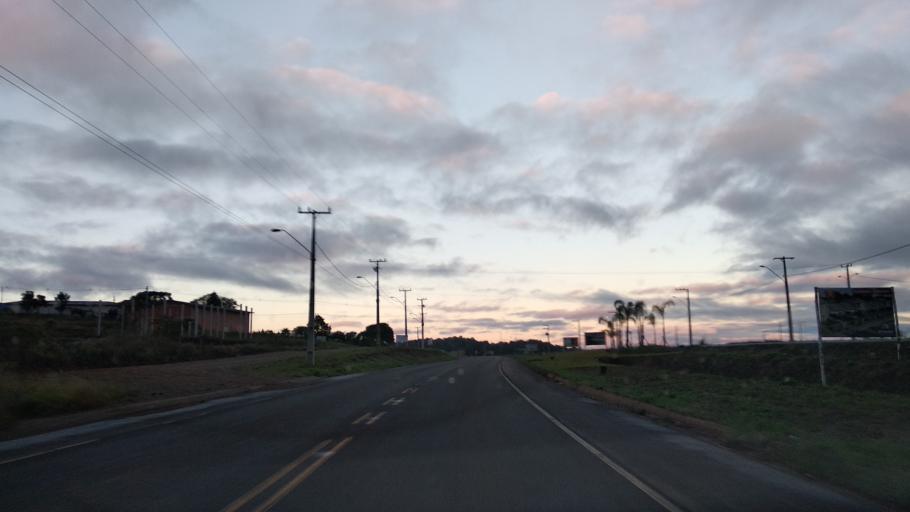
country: BR
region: Santa Catarina
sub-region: Campos Novos
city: Campos Novos
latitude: -27.3772
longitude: -51.2060
